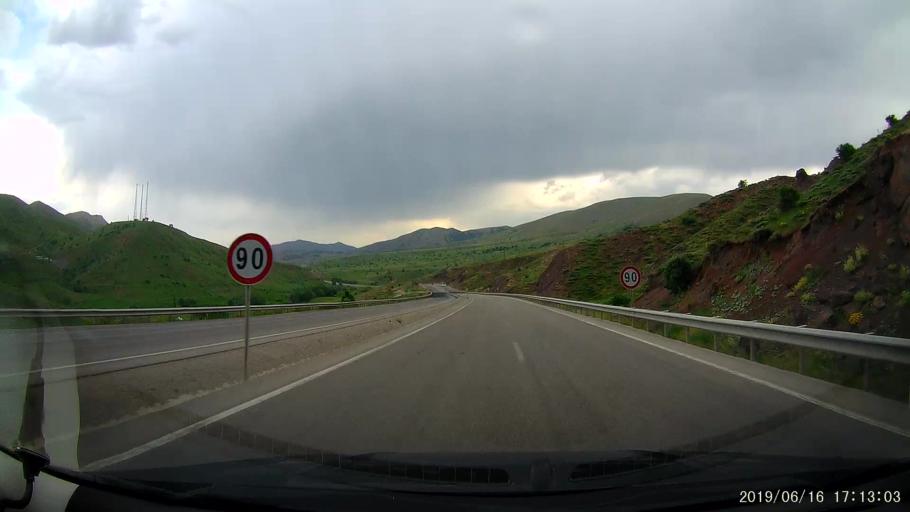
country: TR
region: Erzurum
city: Askale
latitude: 39.8597
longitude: 40.6076
